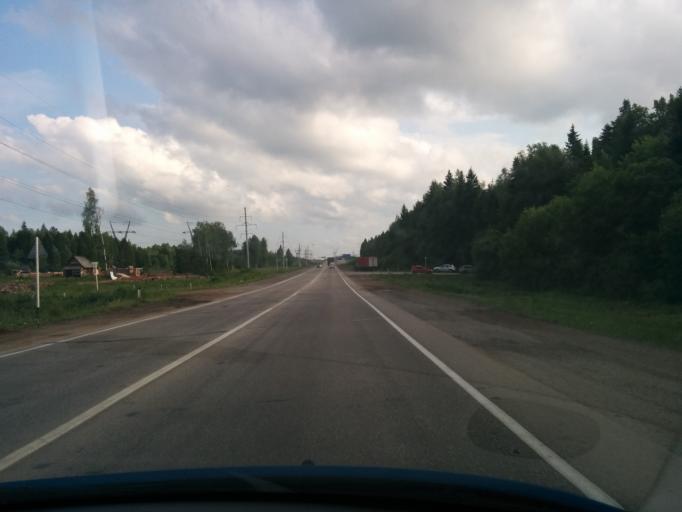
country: RU
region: Perm
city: Novyye Lyady
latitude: 58.0575
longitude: 56.4277
